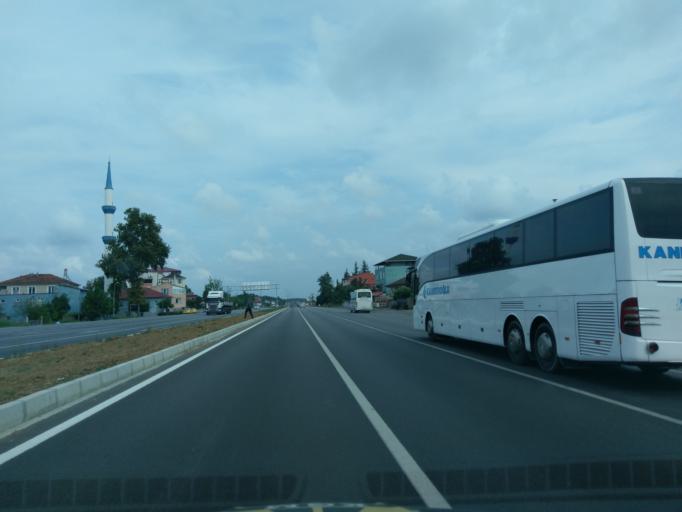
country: TR
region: Samsun
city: Dikbiyik
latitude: 41.2372
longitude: 36.5407
